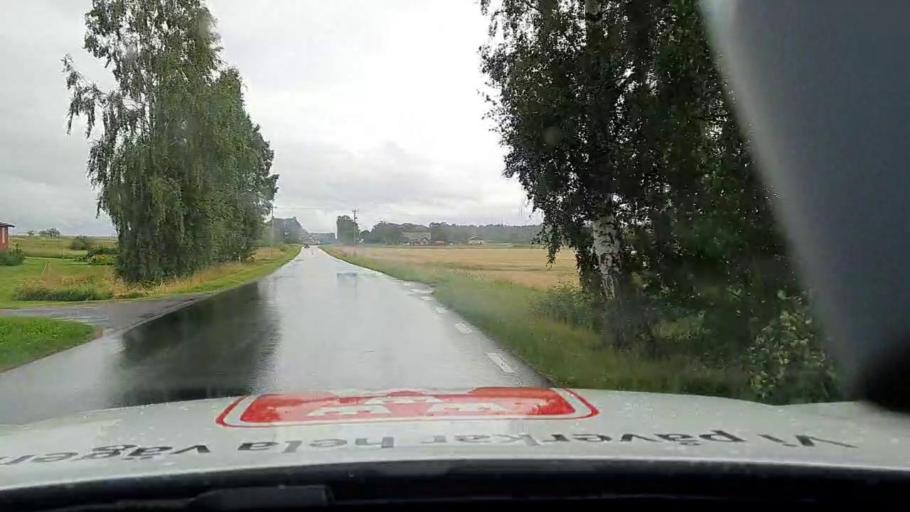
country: SE
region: Vaestra Goetaland
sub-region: Skovde Kommun
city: Stopen
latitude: 58.5580
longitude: 13.9810
